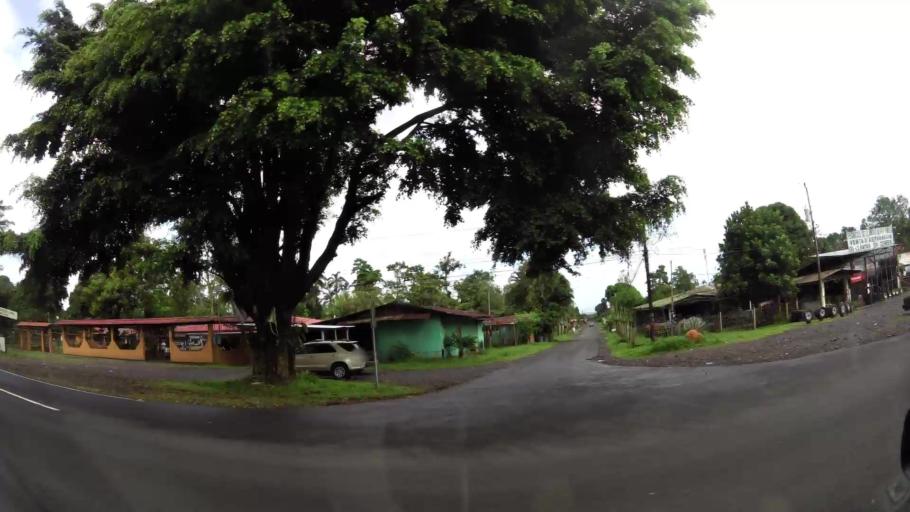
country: CR
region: Limon
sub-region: Canton de Guacimo
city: Guacimo
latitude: 10.2059
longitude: -83.7110
